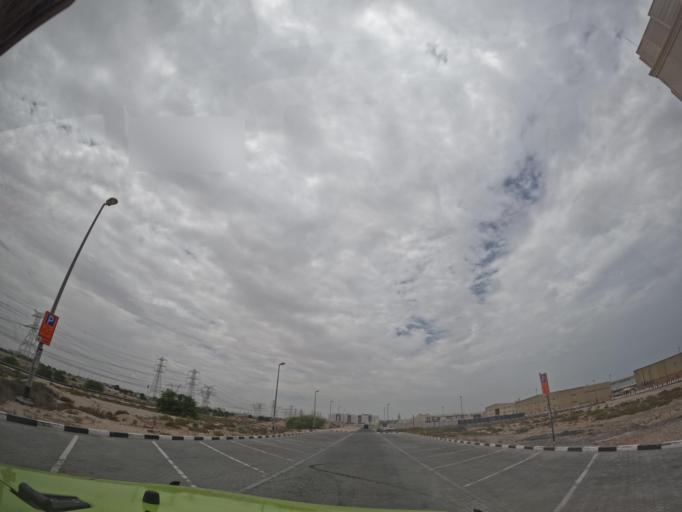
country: AE
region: Ash Shariqah
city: Sharjah
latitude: 25.1867
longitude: 55.3859
